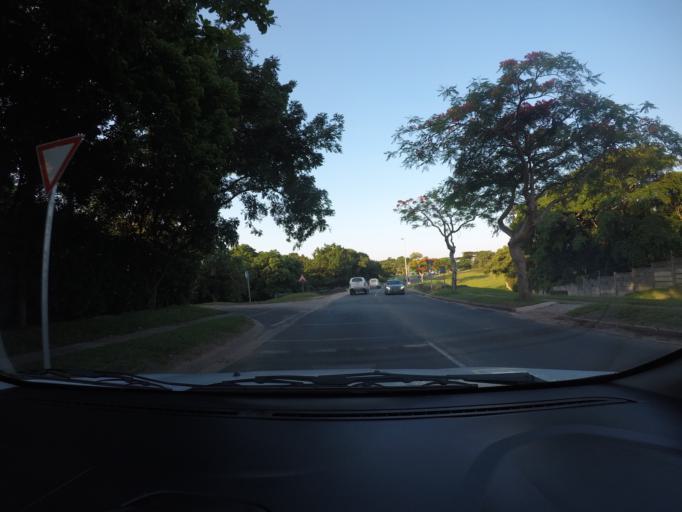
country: ZA
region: KwaZulu-Natal
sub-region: uThungulu District Municipality
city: Richards Bay
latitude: -28.7793
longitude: 32.0998
